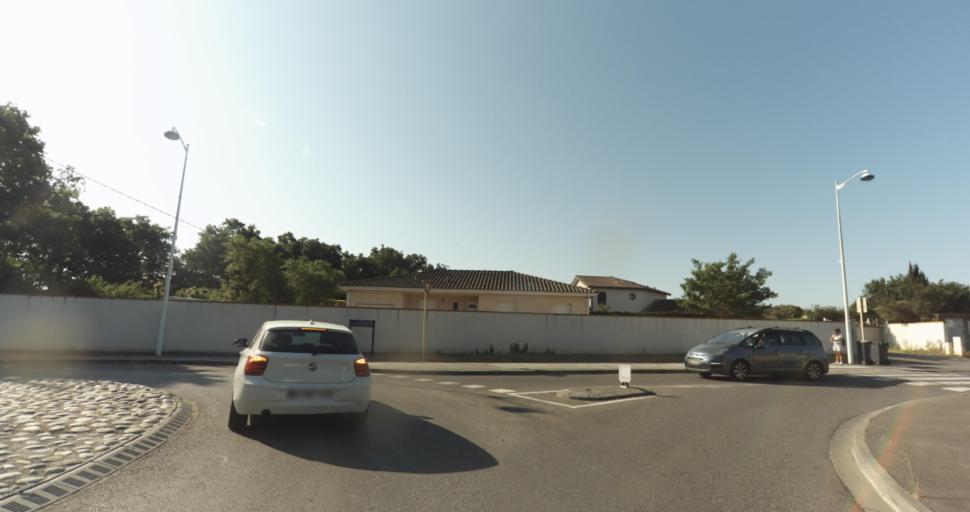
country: FR
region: Midi-Pyrenees
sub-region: Departement de la Haute-Garonne
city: La Salvetat-Saint-Gilles
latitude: 43.5761
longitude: 1.2568
